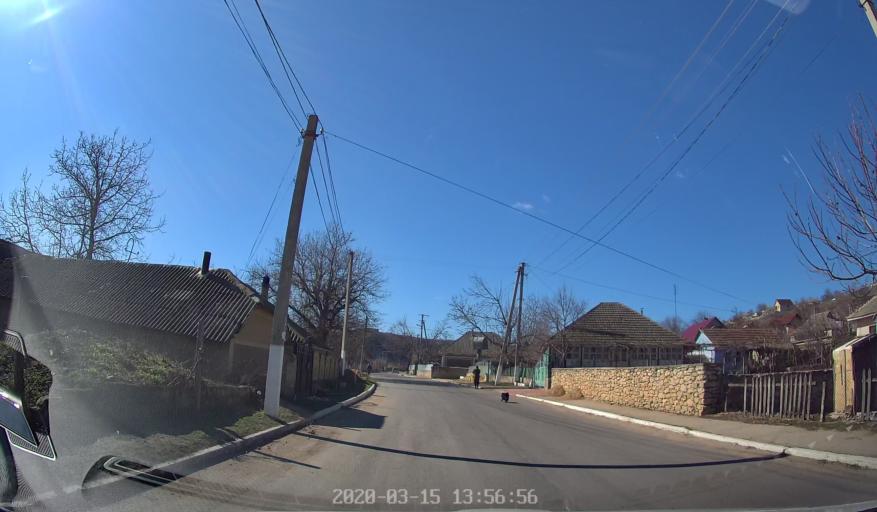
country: MD
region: Telenesti
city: Cocieri
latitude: 47.3104
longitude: 28.9835
